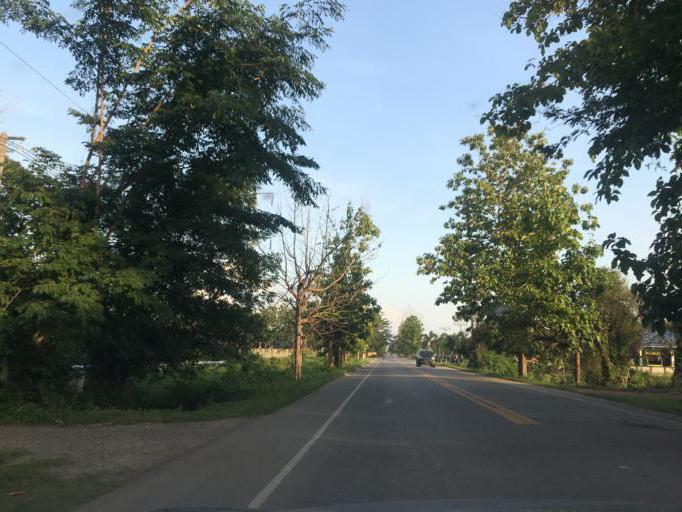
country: TH
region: Phayao
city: Chiang Kham
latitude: 19.5318
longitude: 100.2924
